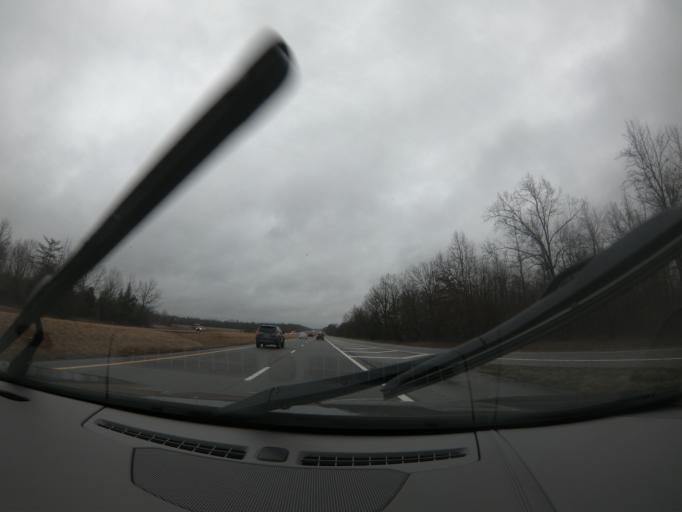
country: US
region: Tennessee
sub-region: Coffee County
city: New Union
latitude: 35.5337
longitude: -86.1598
